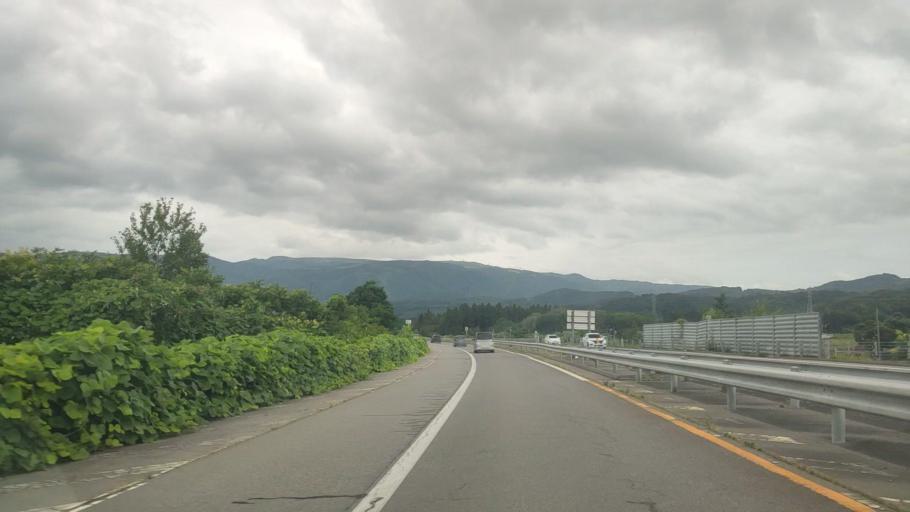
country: JP
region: Hokkaido
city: Nanae
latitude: 41.9202
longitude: 140.6796
